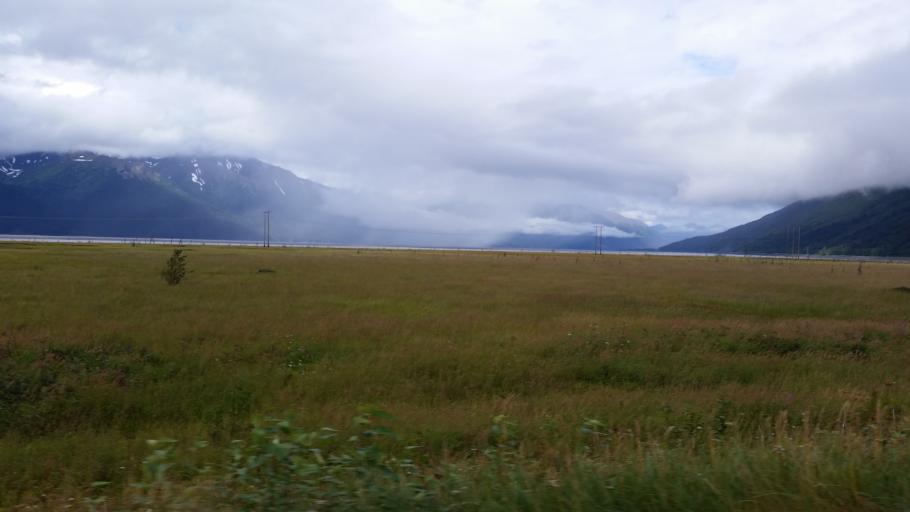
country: US
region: Alaska
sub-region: Anchorage Municipality
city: Girdwood
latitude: 60.9358
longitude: -149.1593
